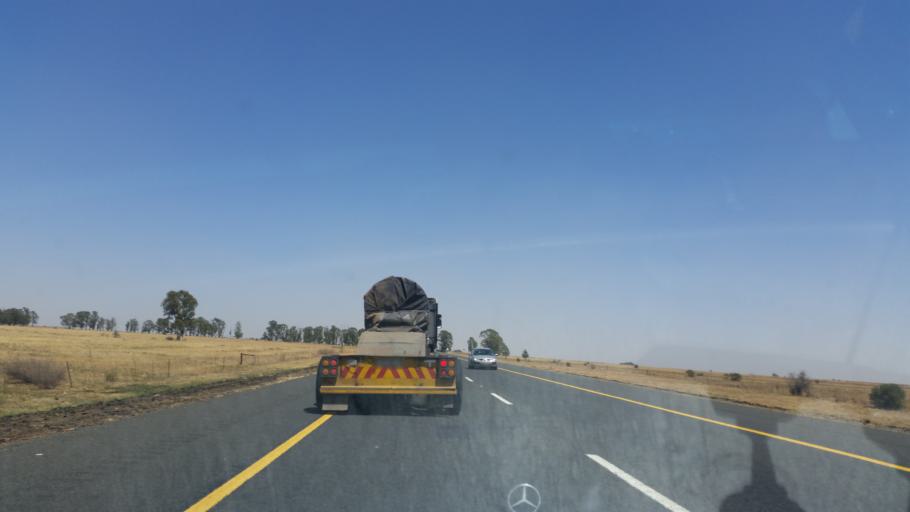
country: ZA
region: Orange Free State
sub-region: Lejweleputswa District Municipality
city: Winburg
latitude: -28.6382
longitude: 26.8939
